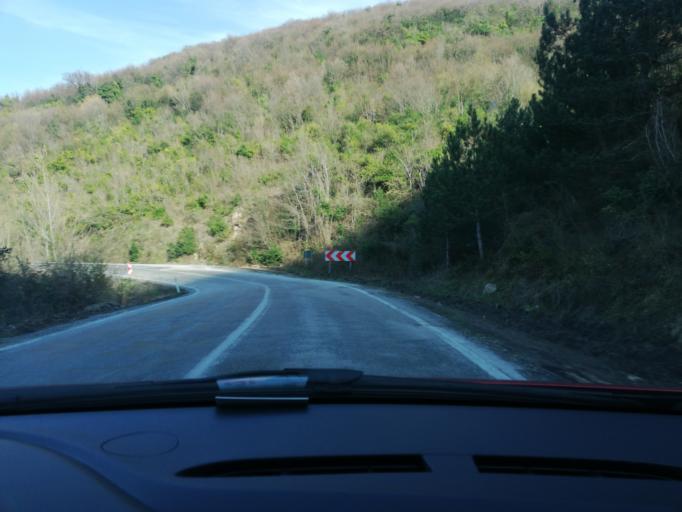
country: TR
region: Bartin
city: Kurucasile
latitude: 41.8445
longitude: 32.7682
